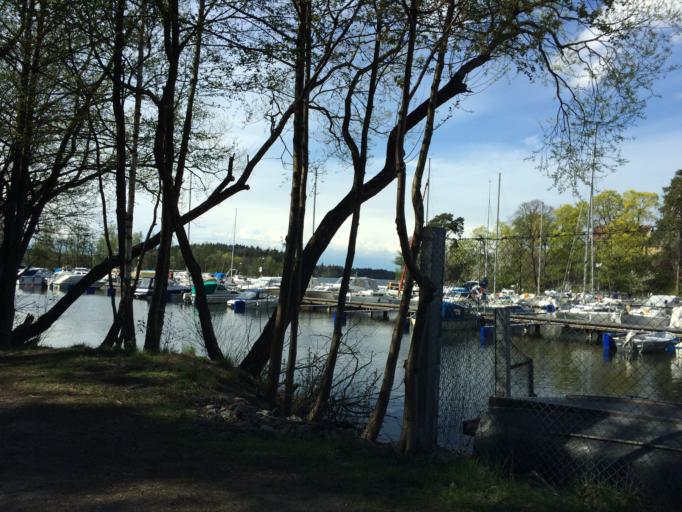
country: SE
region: Stockholm
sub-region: Stockholms Kommun
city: Bromma
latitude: 59.3066
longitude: 17.9597
